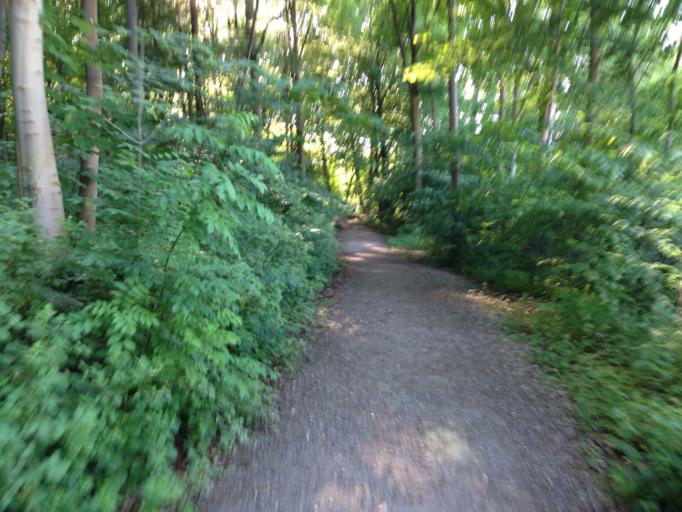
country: DK
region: Capital Region
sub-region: Gentofte Kommune
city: Charlottenlund
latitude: 55.7702
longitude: 12.5652
